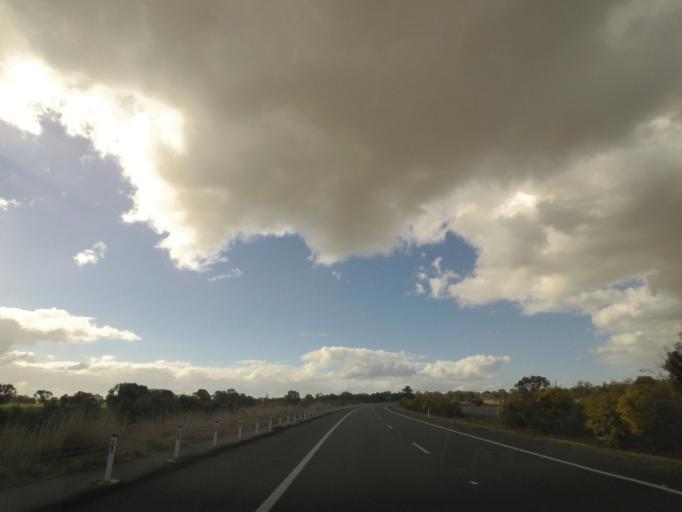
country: AU
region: New South Wales
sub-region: Greater Hume Shire
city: Holbrook
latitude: -35.7119
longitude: 147.3045
